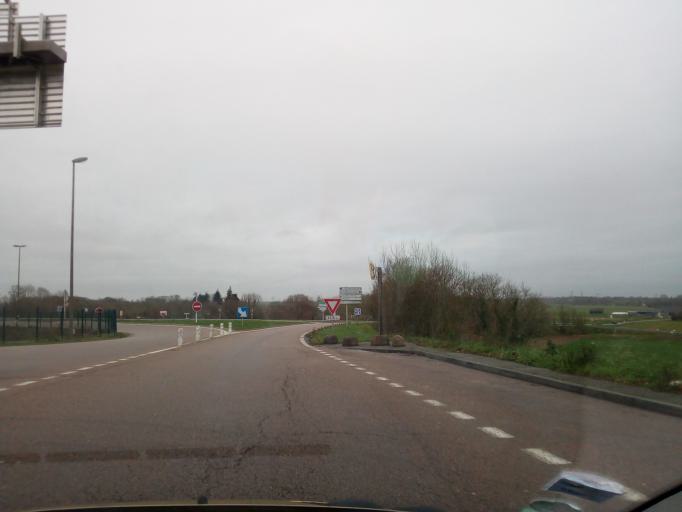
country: FR
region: Haute-Normandie
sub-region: Departement de l'Eure
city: Bourg-Achard
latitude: 49.3670
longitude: 0.8163
